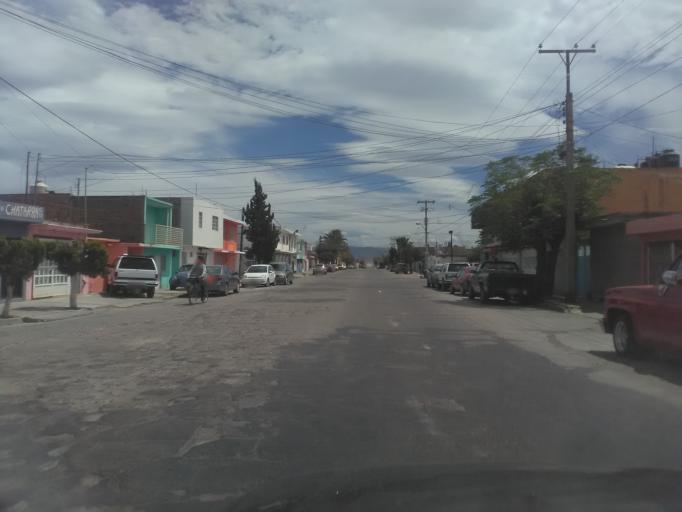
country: MX
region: Durango
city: Victoria de Durango
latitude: 24.0218
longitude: -104.6311
